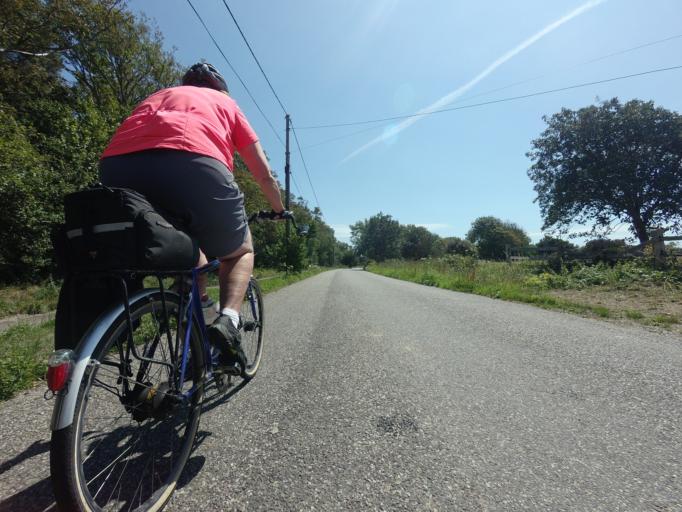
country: GB
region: England
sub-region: Kent
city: Lydd
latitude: 50.9554
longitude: 0.9038
